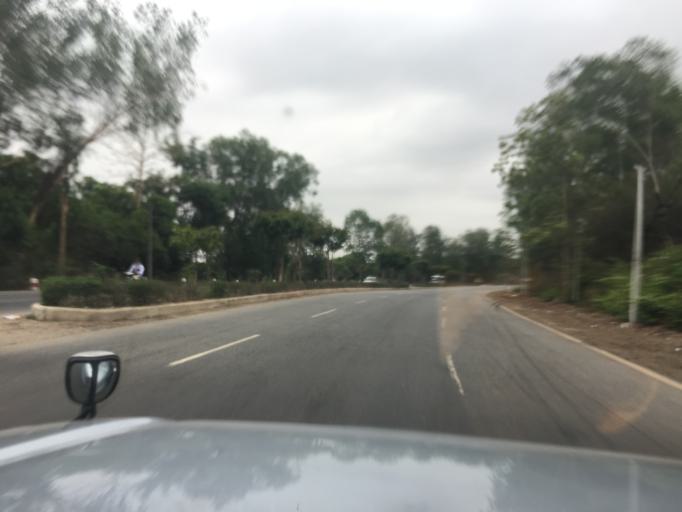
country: MM
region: Bago
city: Thanatpin
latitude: 17.2119
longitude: 96.4173
